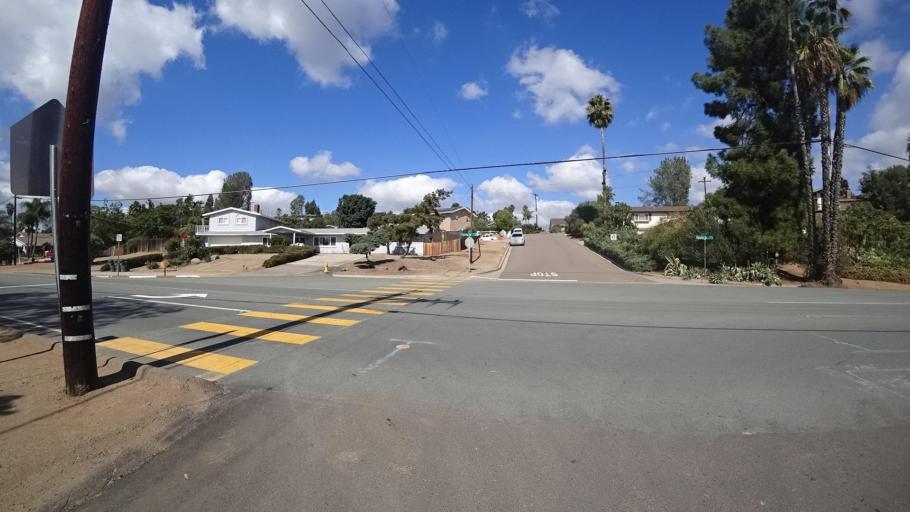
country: US
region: California
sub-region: San Diego County
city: Rancho San Diego
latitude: 32.7621
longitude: -116.9451
